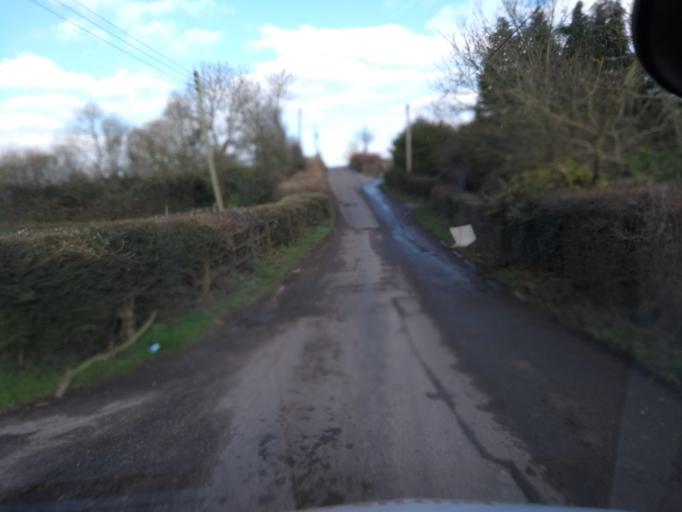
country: GB
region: England
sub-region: Somerset
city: Creech Saint Michael
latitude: 50.9612
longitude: -3.0241
